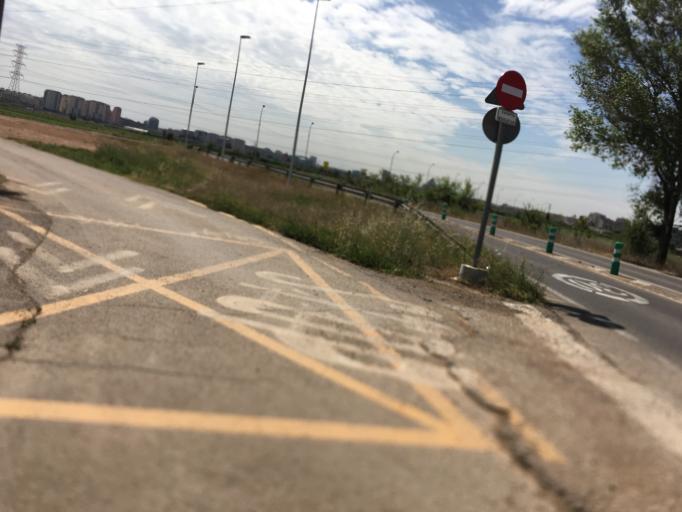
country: ES
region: Valencia
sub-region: Provincia de Valencia
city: Paterna
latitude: 39.4942
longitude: -0.4187
